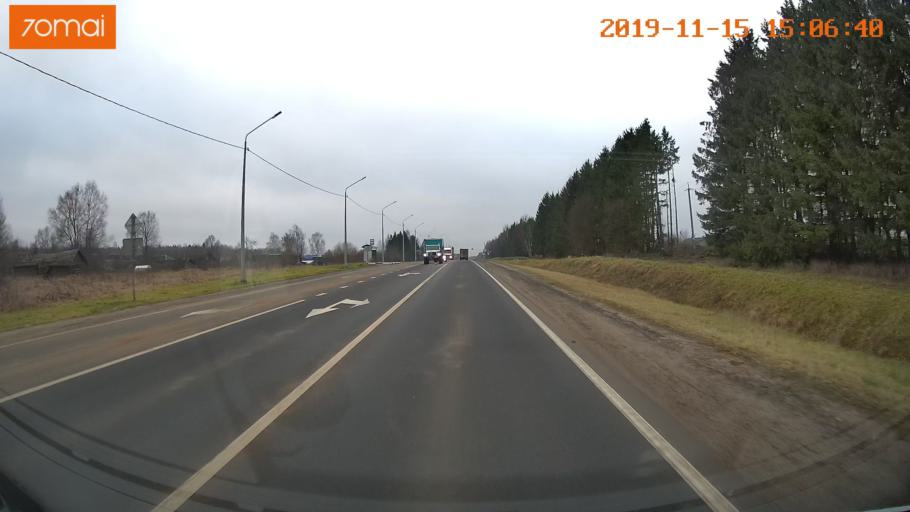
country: RU
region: Jaroslavl
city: Prechistoye
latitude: 58.3906
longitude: 40.3072
